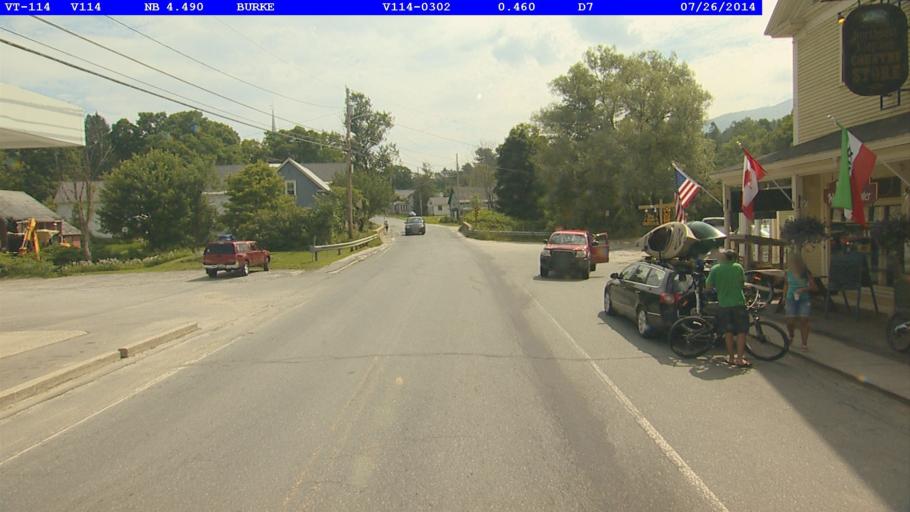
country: US
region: Vermont
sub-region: Caledonia County
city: Lyndonville
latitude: 44.5881
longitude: -71.9450
